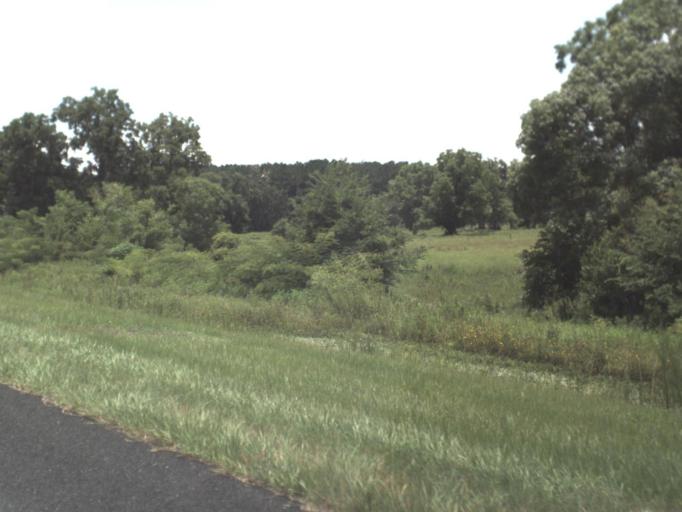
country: US
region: Florida
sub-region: Levy County
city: Williston
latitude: 29.3876
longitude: -82.4622
